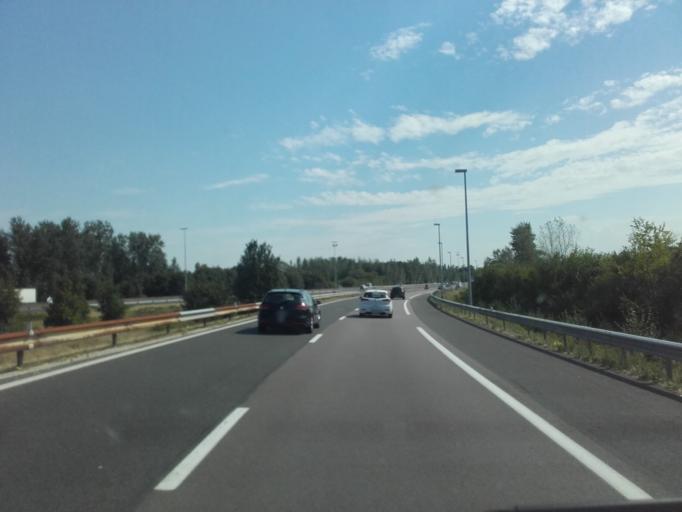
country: FR
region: Bourgogne
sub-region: Departement de la Cote-d'Or
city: Beaune
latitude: 47.0269
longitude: 4.8725
